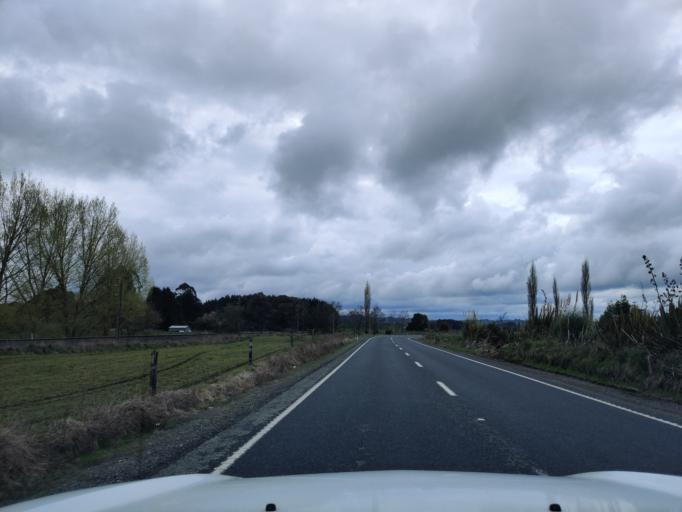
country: NZ
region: Waikato
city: Turangi
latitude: -39.0240
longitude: 175.3807
